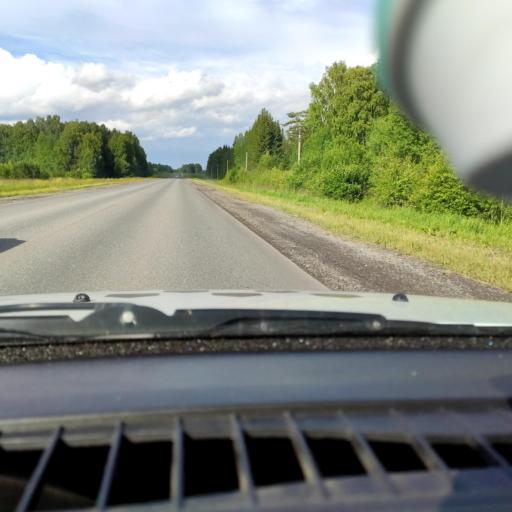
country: RU
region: Perm
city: Orda
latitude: 57.2381
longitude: 56.9808
